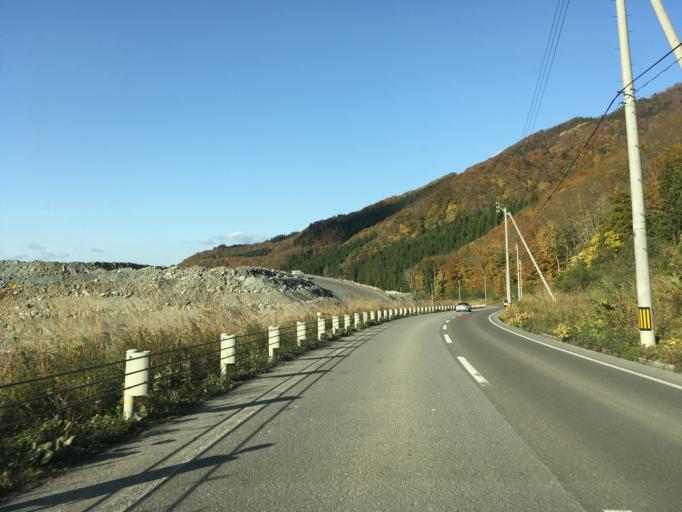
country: JP
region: Akita
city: Yuzawa
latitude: 39.0528
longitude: 140.7228
